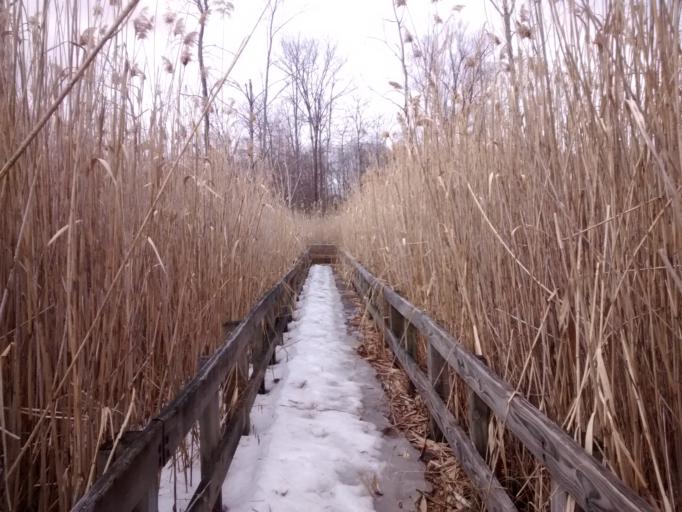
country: US
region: New York
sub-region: Schenectady County
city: Niskayuna
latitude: 42.8184
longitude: -73.8843
